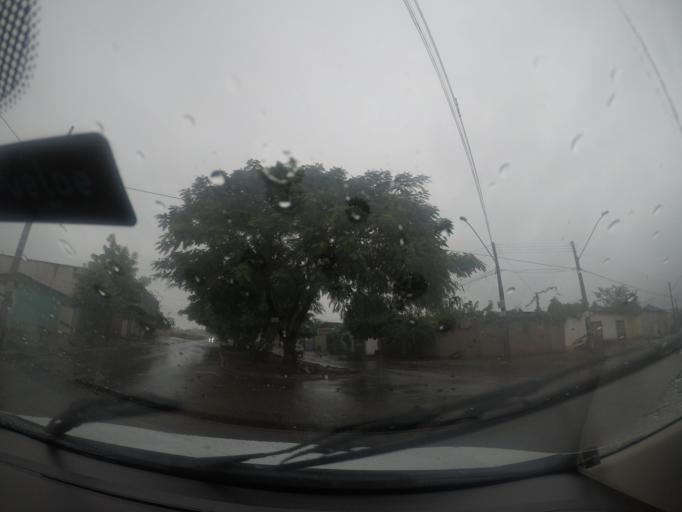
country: BR
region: Goias
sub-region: Goiania
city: Goiania
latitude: -16.5949
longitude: -49.3249
